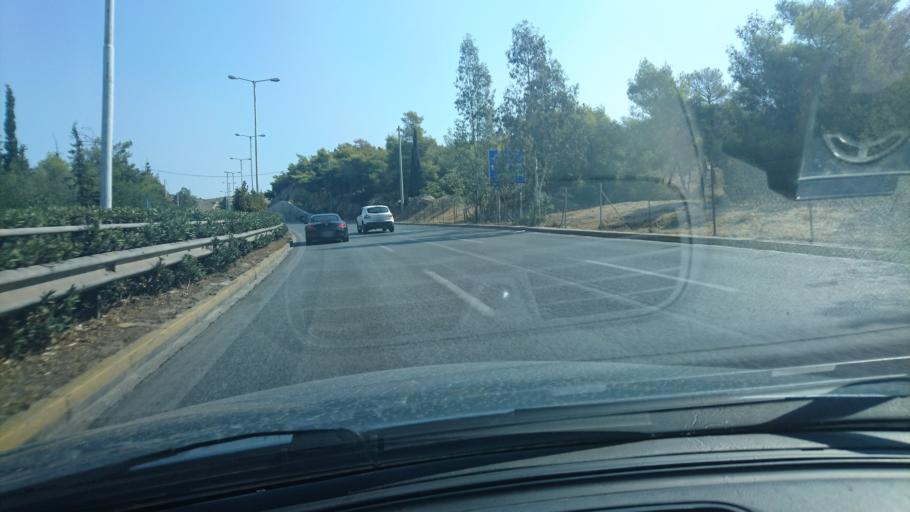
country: GR
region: Attica
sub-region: Nomarchia Athinas
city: Kaisariani
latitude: 37.9539
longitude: 23.7717
